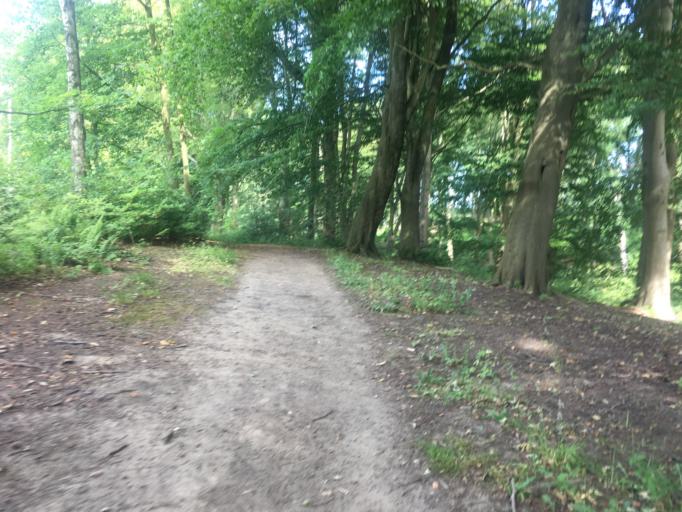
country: GB
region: England
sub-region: Sunderland
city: Washington
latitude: 54.8739
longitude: -1.5352
